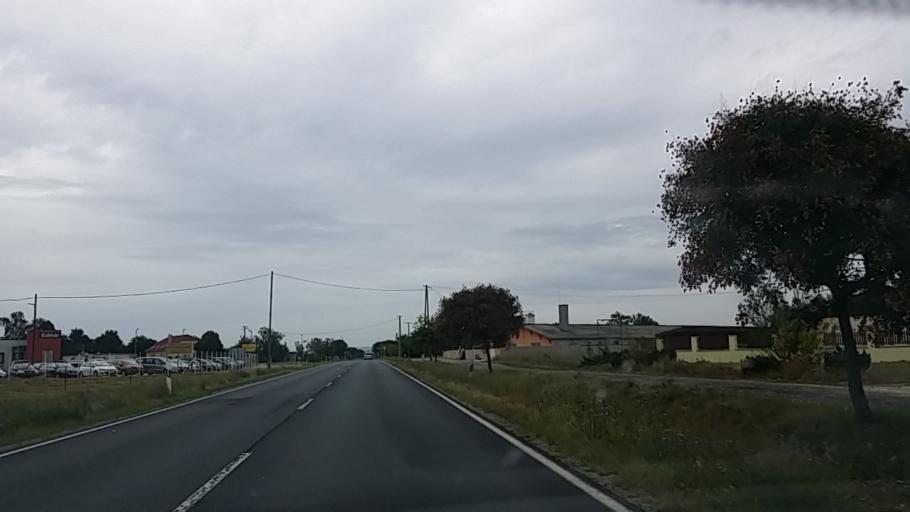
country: HU
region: Gyor-Moson-Sopron
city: Fertoszentmiklos
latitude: 47.5880
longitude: 16.8651
